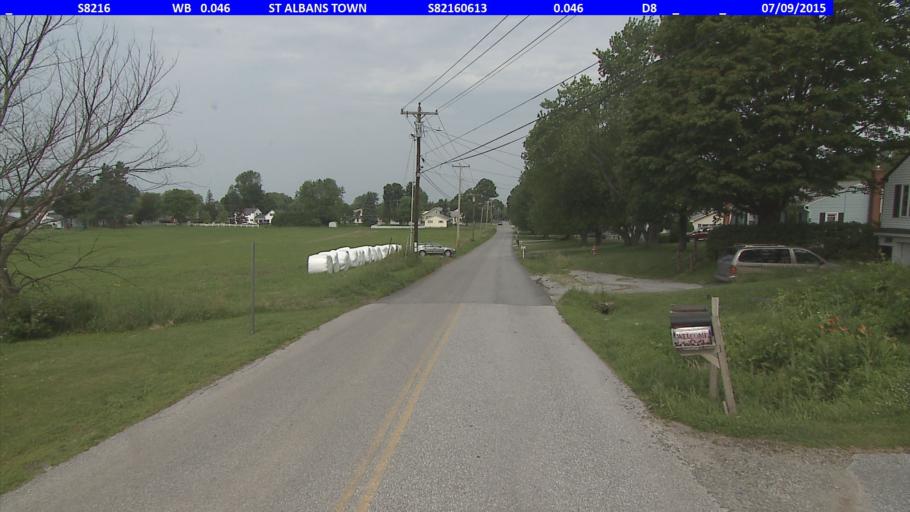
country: US
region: Vermont
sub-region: Franklin County
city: Saint Albans
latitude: 44.8029
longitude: -73.0725
